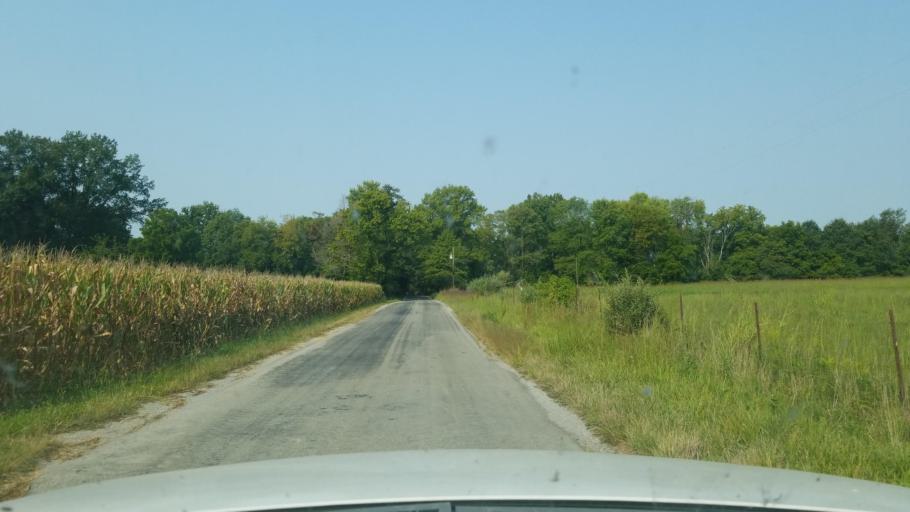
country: US
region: Illinois
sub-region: Saline County
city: Carrier Mills
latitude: 37.7905
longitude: -88.6781
